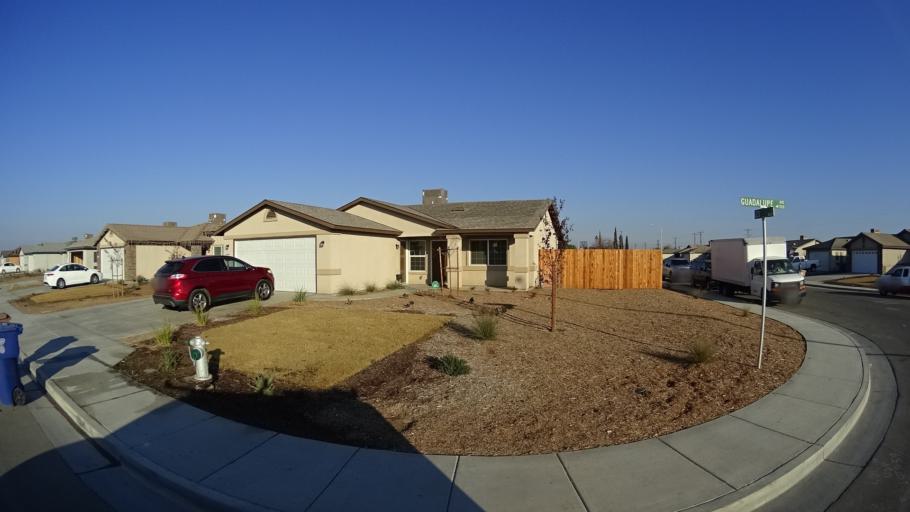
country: US
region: California
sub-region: Kern County
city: Greenfield
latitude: 35.2981
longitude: -118.9914
